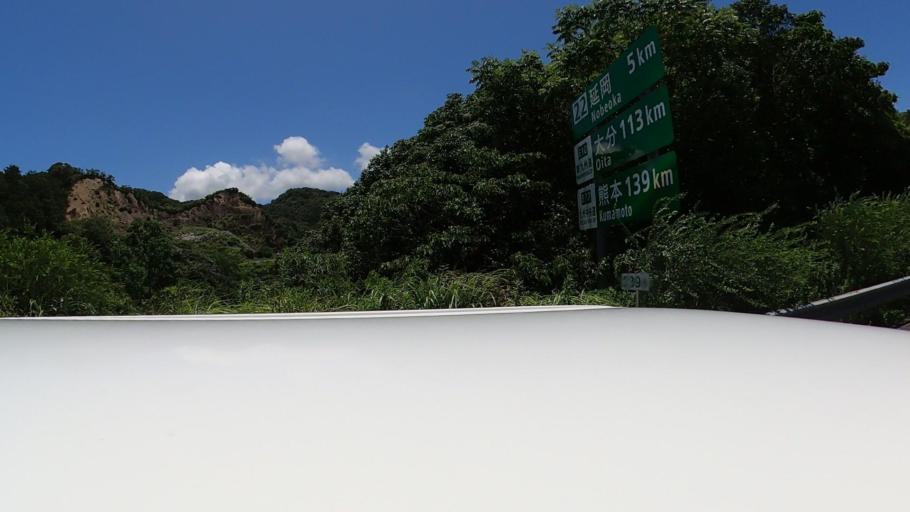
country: JP
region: Miyazaki
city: Nobeoka
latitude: 32.5379
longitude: 131.6595
